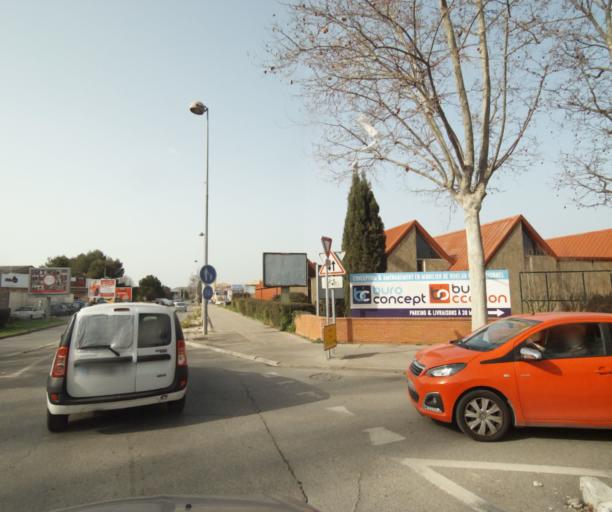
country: FR
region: Provence-Alpes-Cote d'Azur
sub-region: Departement des Bouches-du-Rhone
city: Les Pennes-Mirabeau
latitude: 43.4205
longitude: 5.2890
